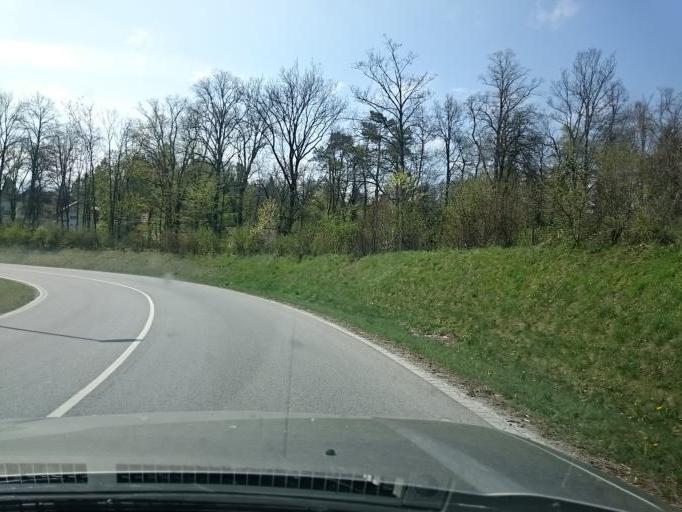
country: DE
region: Bavaria
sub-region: Upper Bavaria
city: Murnau am Staffelsee
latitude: 47.6797
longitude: 11.1935
